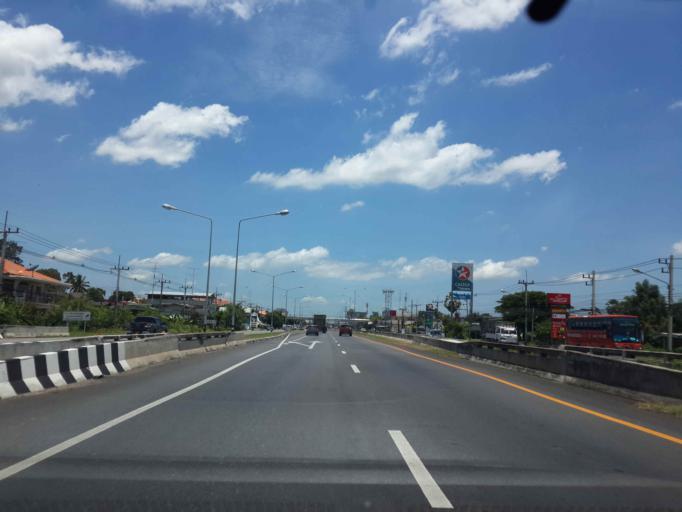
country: TH
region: Phetchaburi
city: Ban Lat
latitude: 13.0665
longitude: 99.9460
